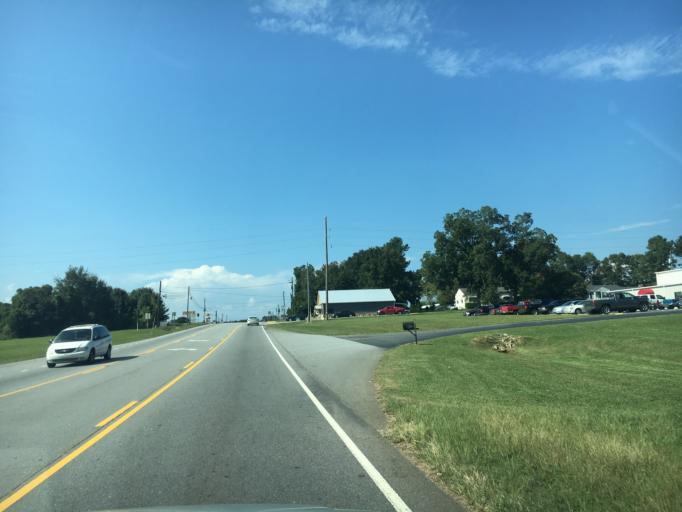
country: US
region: Georgia
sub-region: Franklin County
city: Lavonia
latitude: 34.4209
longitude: -83.1020
